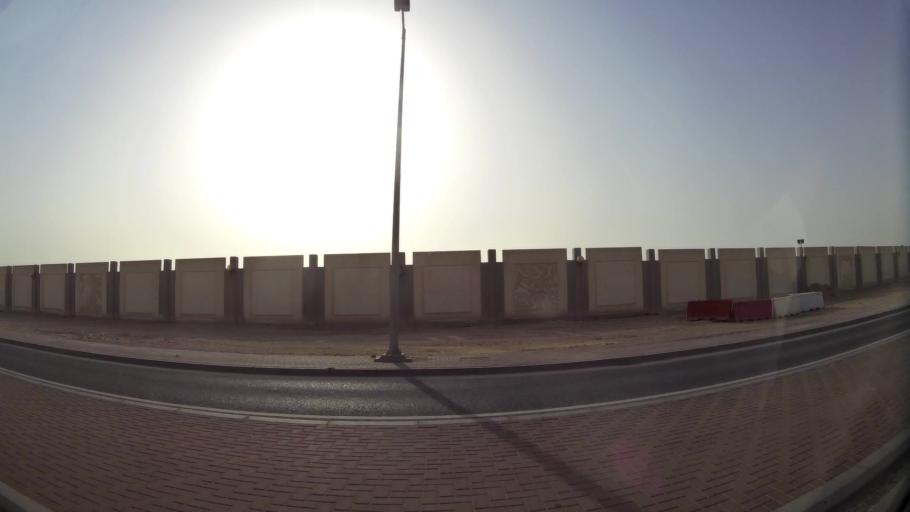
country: QA
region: Baladiyat ar Rayyan
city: Ar Rayyan
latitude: 25.2468
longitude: 51.4379
